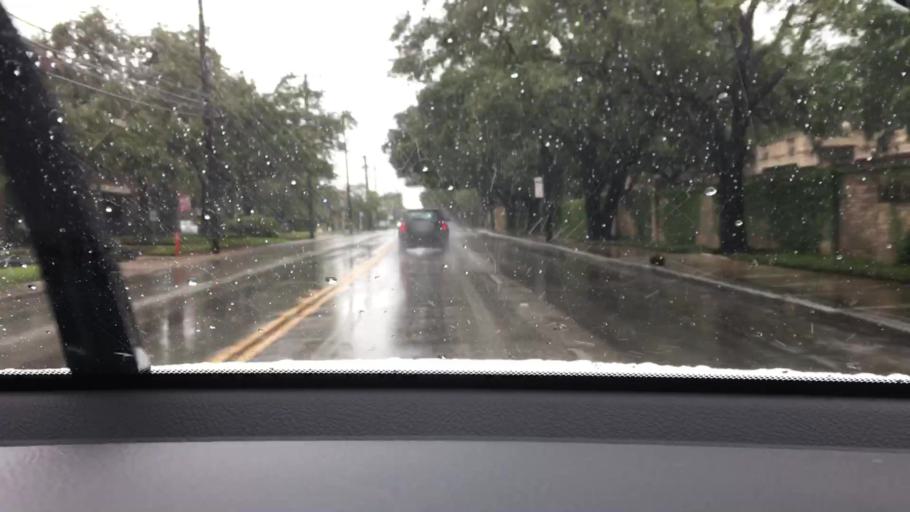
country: US
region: Texas
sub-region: Bexar County
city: Alamo Heights
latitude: 29.5023
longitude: -98.4666
